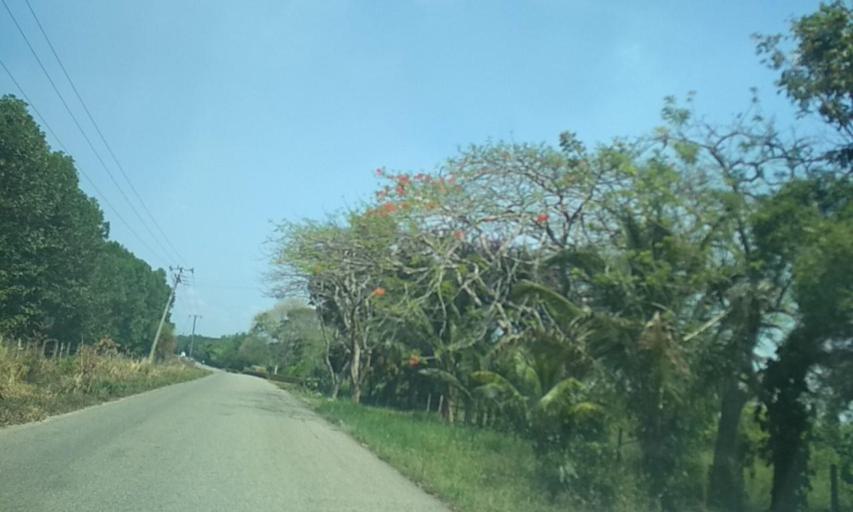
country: MX
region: Tabasco
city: Huimanguillo
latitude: 17.8001
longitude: -93.4717
